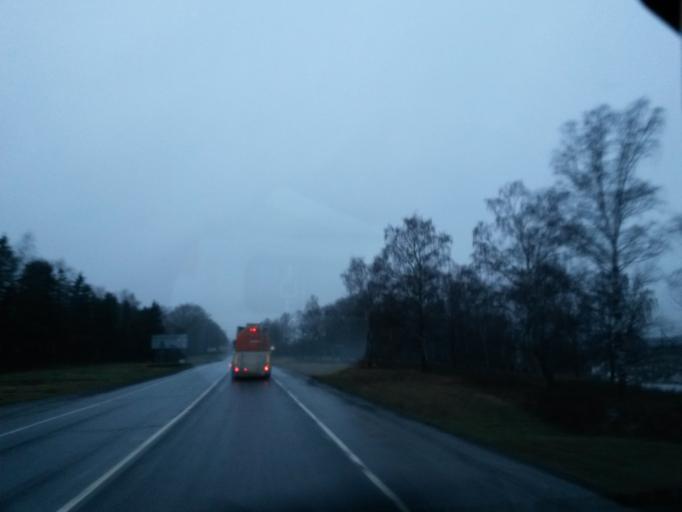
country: RU
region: Moskovskaya
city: Klimovsk
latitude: 55.3318
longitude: 37.5951
